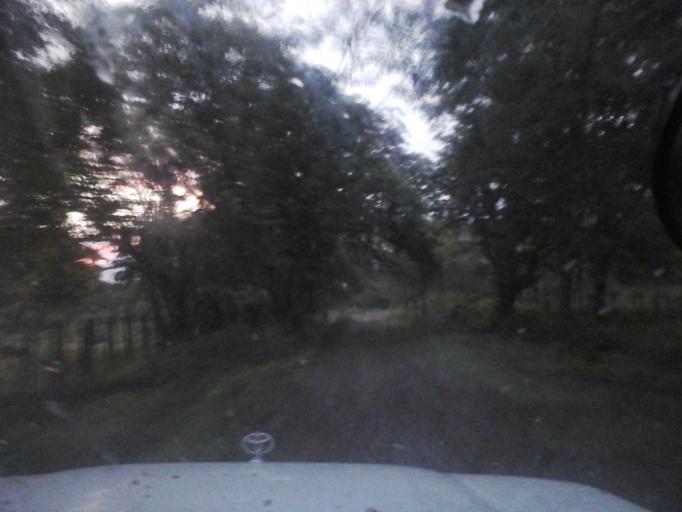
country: CO
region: Cesar
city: Agustin Codazzi
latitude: 10.1560
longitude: -73.2115
